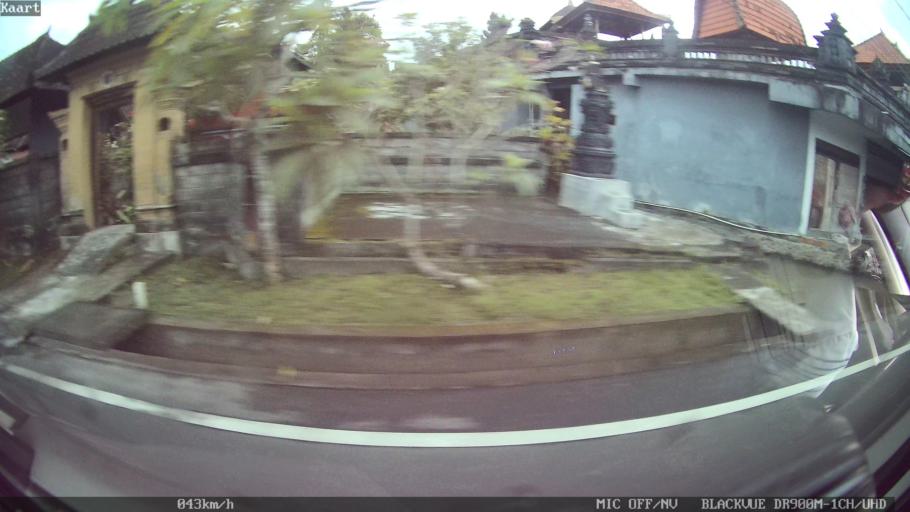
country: ID
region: Bali
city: Banjar Cemenggon
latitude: -8.5248
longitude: 115.1861
